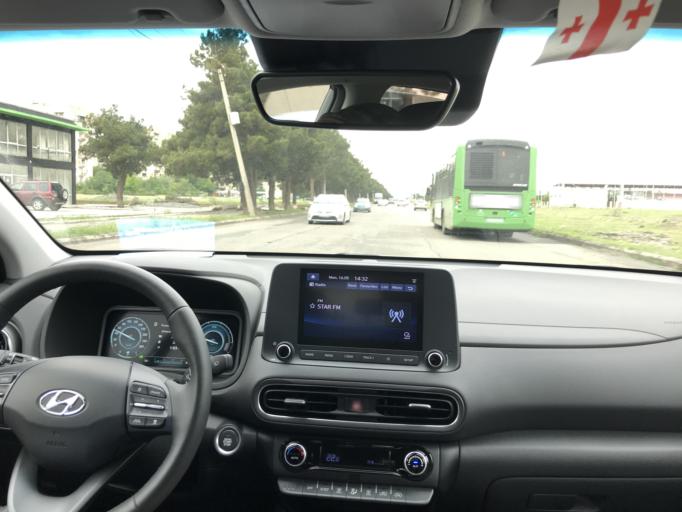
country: GE
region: Kvemo Kartli
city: Rust'avi
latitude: 41.5690
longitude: 44.9965
